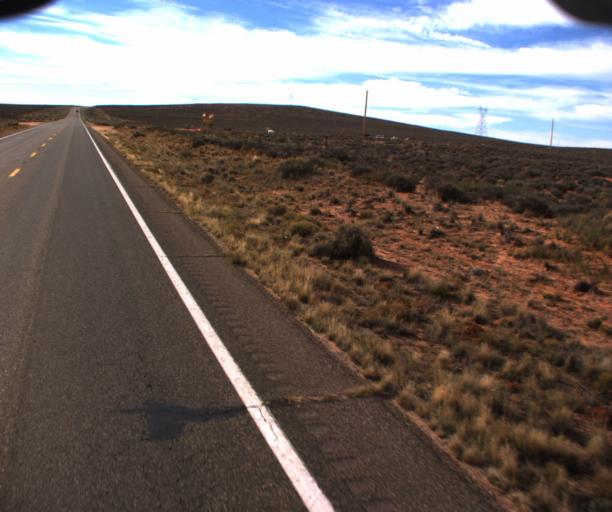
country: US
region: Arizona
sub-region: Coconino County
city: LeChee
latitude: 36.8215
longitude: -111.3081
